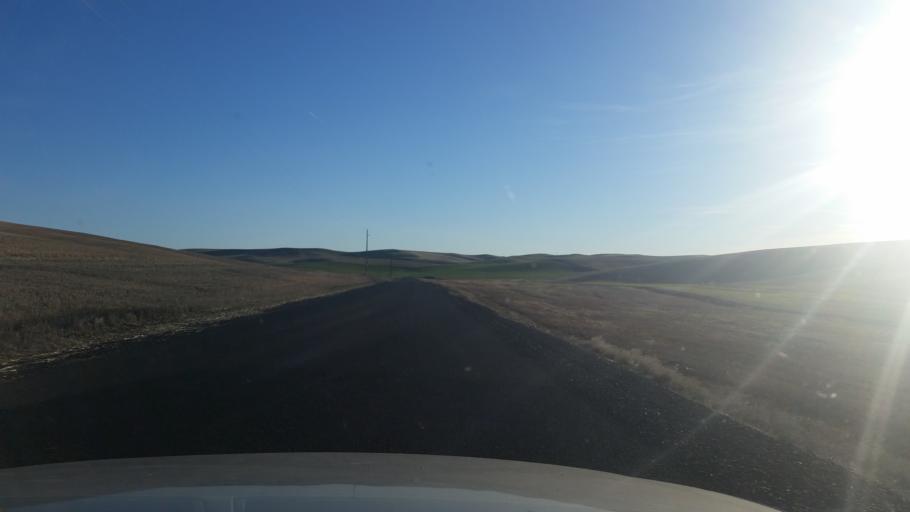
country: US
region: Washington
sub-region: Spokane County
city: Cheney
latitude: 47.3469
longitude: -117.4522
